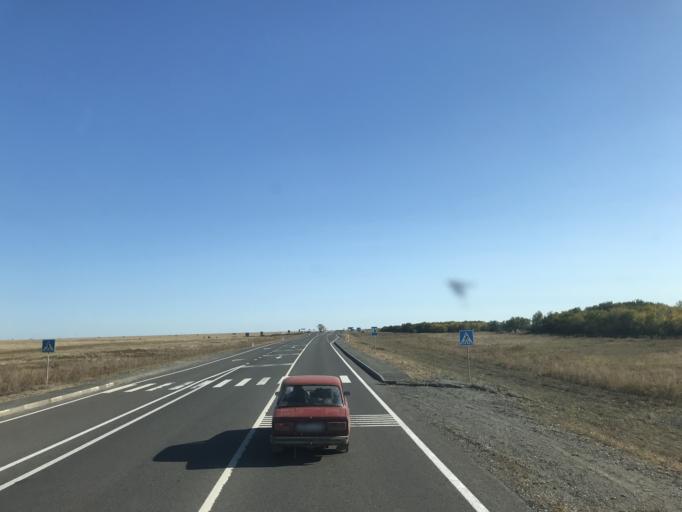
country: KZ
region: Pavlodar
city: Aksu
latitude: 52.0198
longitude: 77.2302
